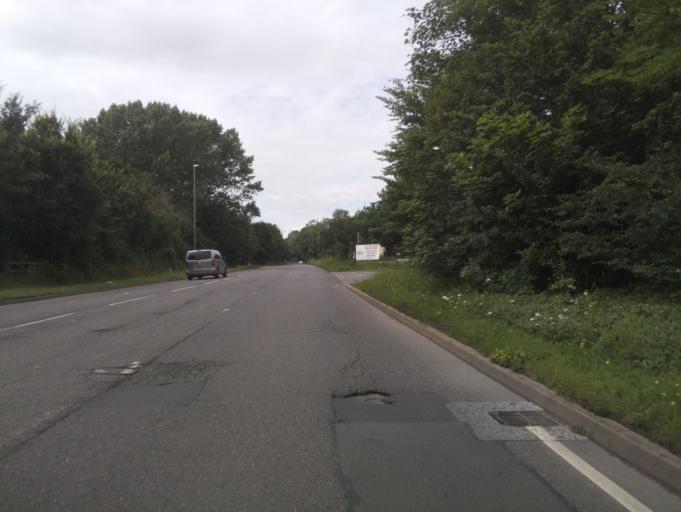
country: GB
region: England
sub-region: Northamptonshire
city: Corby
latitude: 52.5113
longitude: -0.6928
